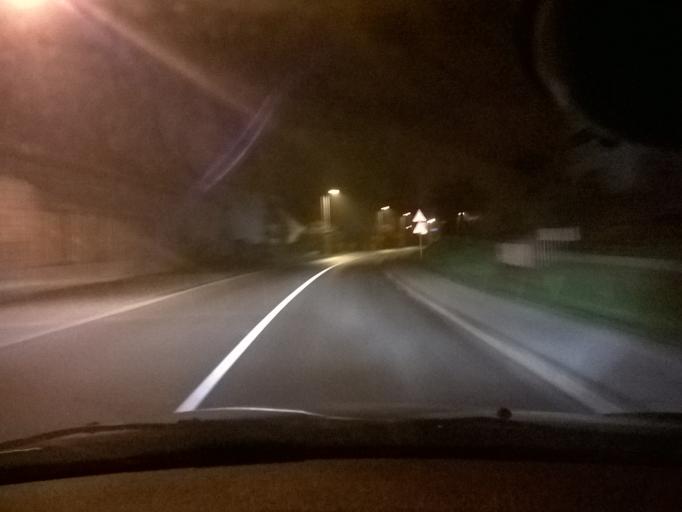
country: HR
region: Krapinsko-Zagorska
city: Zabok
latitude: 46.0827
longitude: 15.9060
